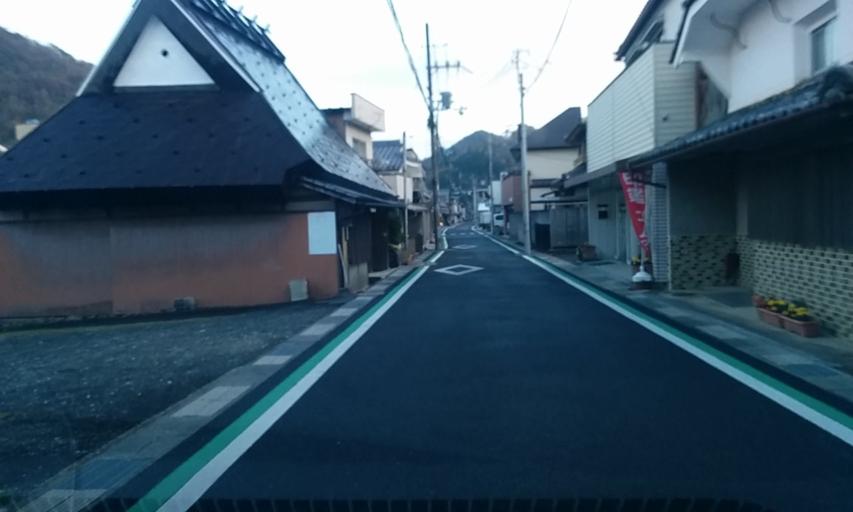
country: JP
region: Kyoto
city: Kameoka
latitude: 35.1539
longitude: 135.4256
